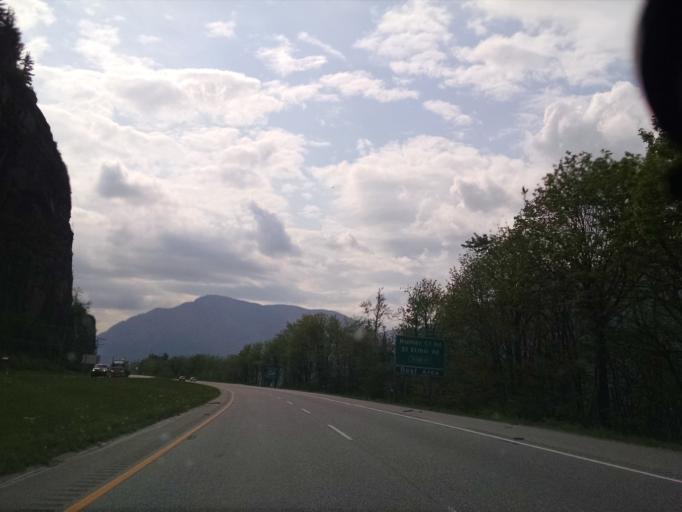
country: CA
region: British Columbia
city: Hope
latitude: 49.3625
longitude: -121.5632
